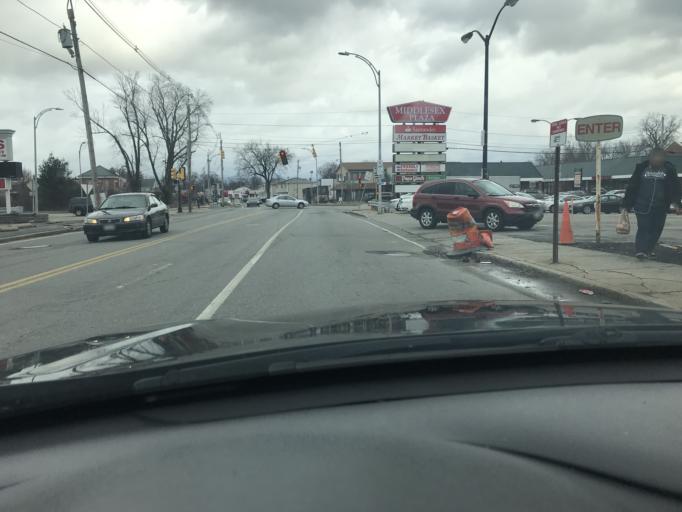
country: US
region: Massachusetts
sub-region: Middlesex County
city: Chelmsford
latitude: 42.6347
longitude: -71.3565
